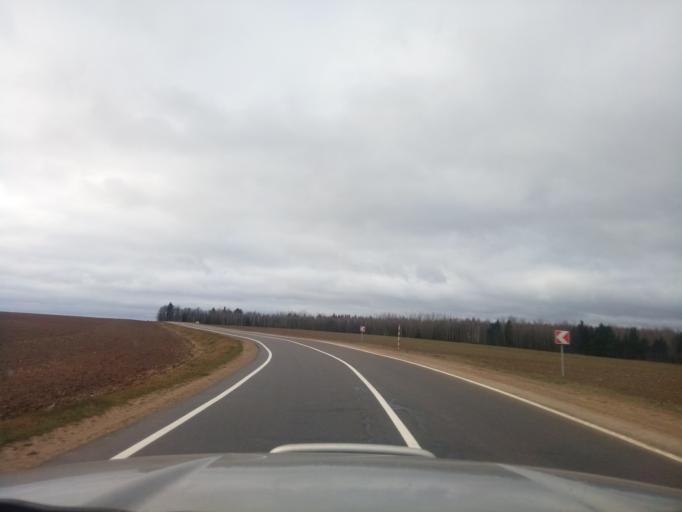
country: BY
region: Minsk
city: Kapyl'
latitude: 53.2076
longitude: 27.2269
